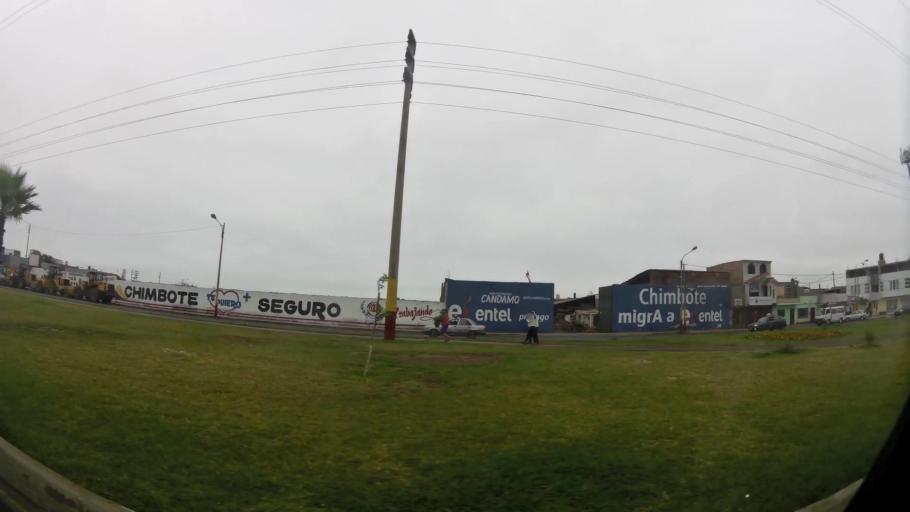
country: PE
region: Ancash
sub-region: Provincia de Santa
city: Chimbote
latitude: -9.0828
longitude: -78.5757
